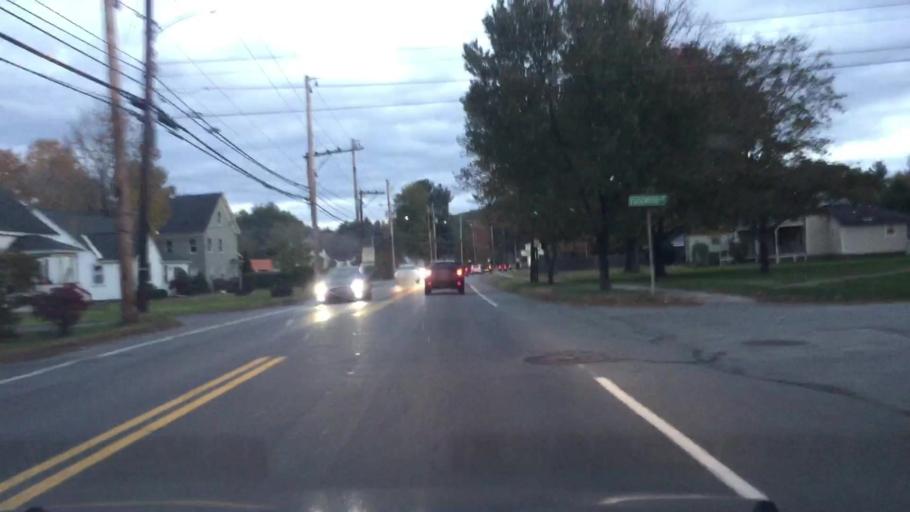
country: US
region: New Hampshire
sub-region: Cheshire County
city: Keene
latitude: 42.9143
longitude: -72.2686
